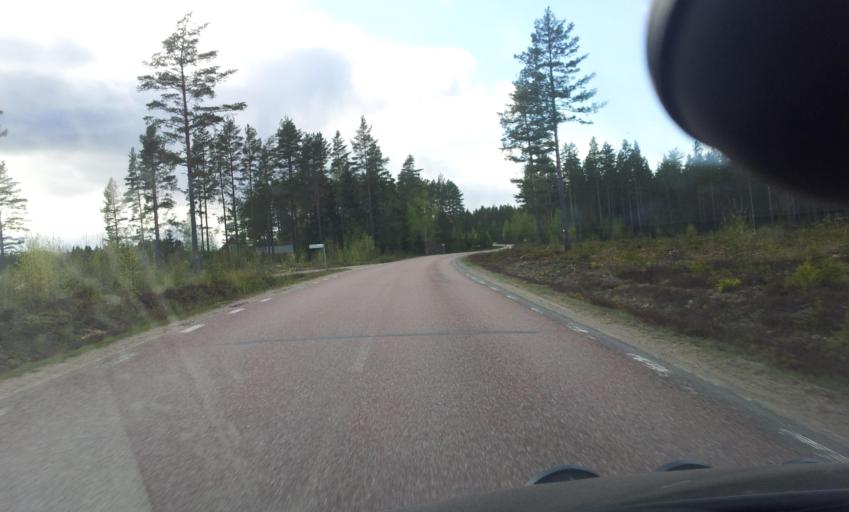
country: SE
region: Gaevleborg
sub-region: Bollnas Kommun
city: Kilafors
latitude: 61.3589
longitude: 16.6724
